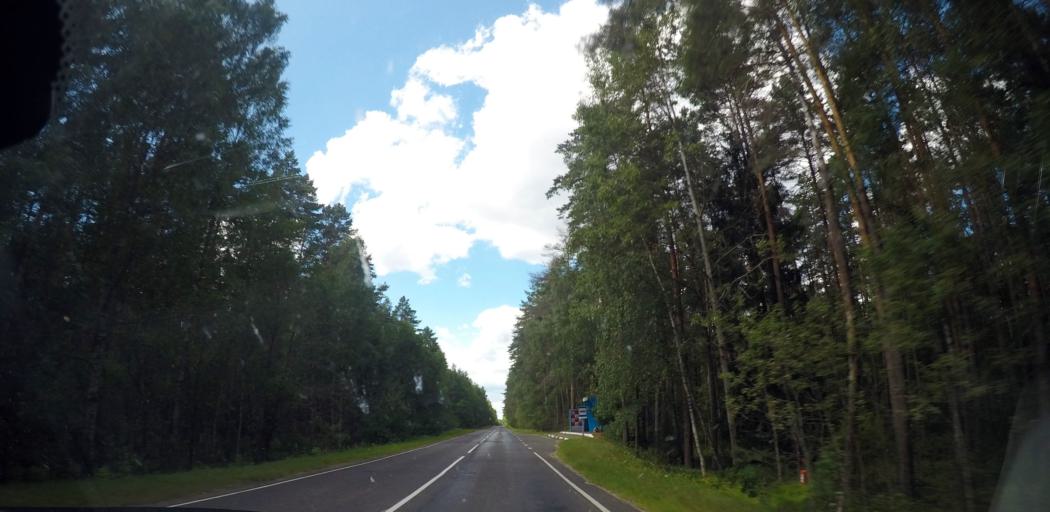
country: BY
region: Grodnenskaya
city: Skidal'
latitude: 53.8426
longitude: 24.2117
